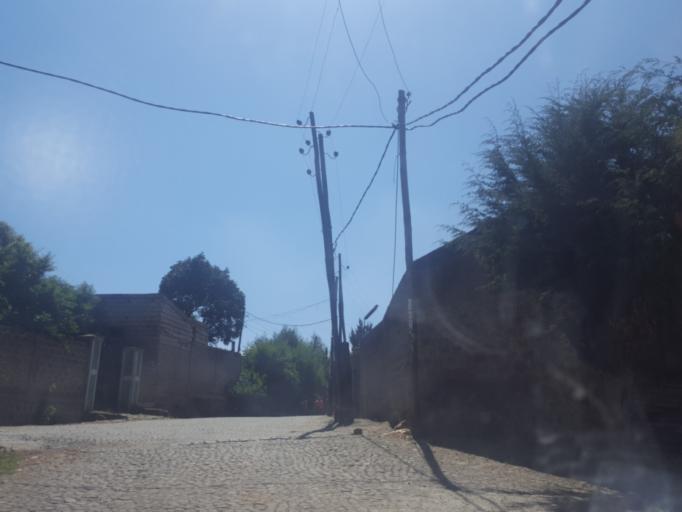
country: ET
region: Adis Abeba
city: Addis Ababa
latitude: 9.0694
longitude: 38.7345
